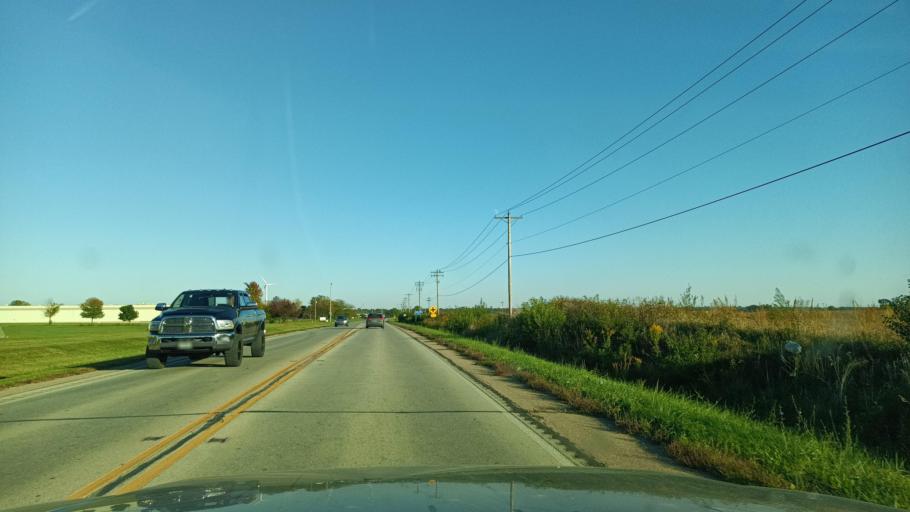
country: US
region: Illinois
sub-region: Champaign County
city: Champaign
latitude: 40.1527
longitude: -88.2993
